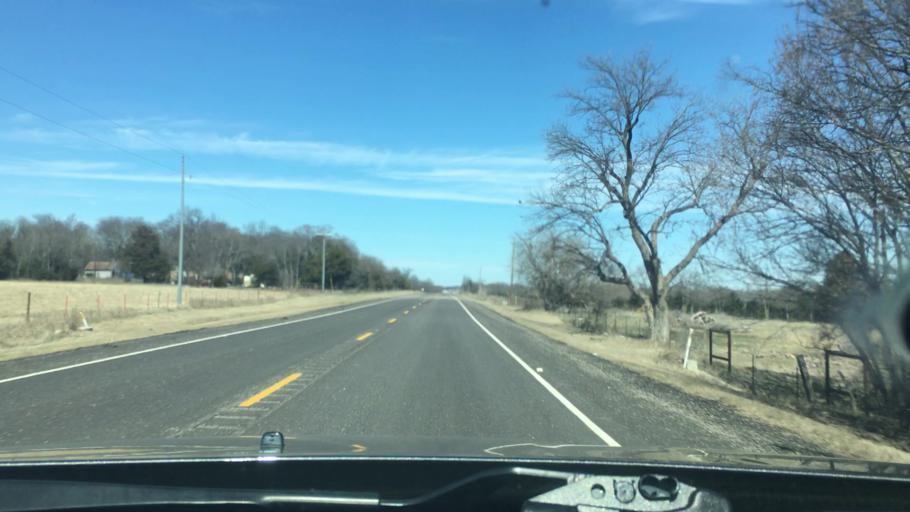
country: US
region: Oklahoma
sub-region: Murray County
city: Sulphur
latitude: 34.3531
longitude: -96.9508
